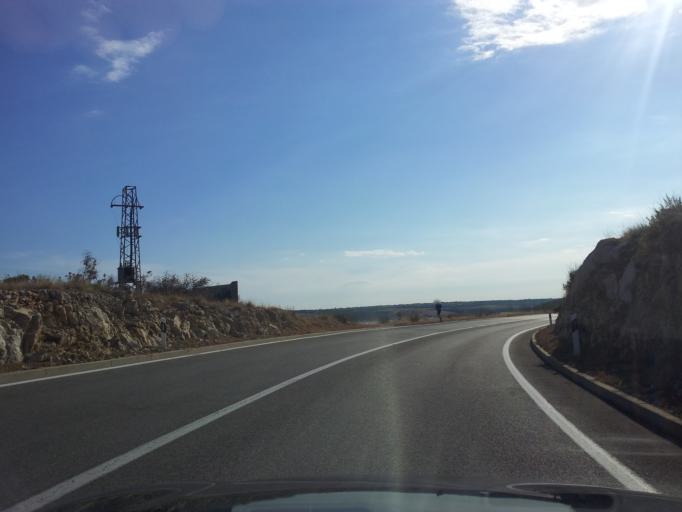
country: HR
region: Zadarska
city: Posedarje
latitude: 44.2223
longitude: 15.5289
